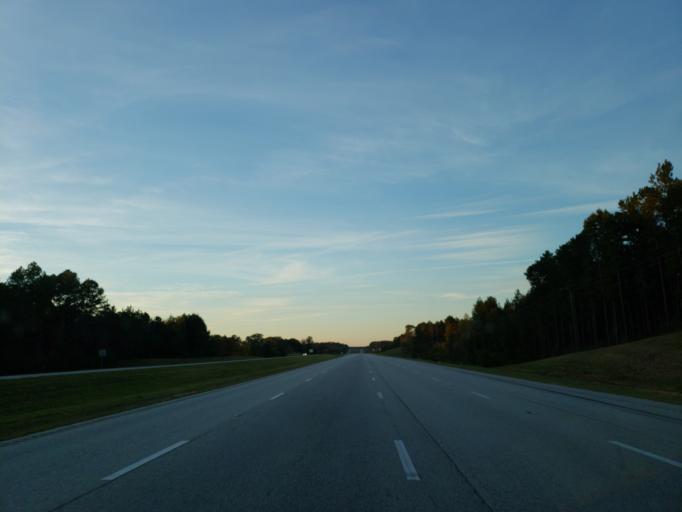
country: US
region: Mississippi
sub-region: Wayne County
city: Belmont
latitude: 31.4601
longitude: -88.4684
